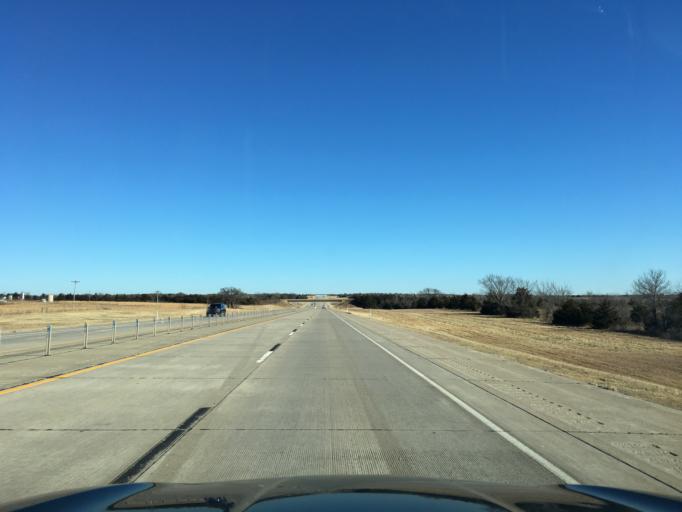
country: US
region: Oklahoma
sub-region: Payne County
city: Yale
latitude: 36.2250
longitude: -96.6837
